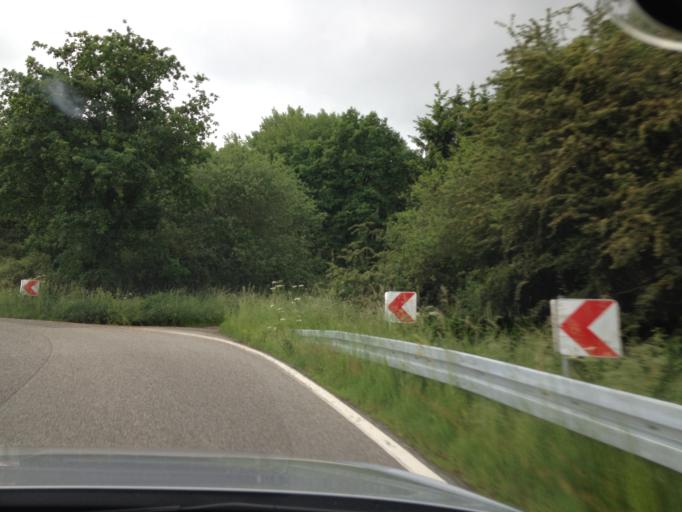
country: DE
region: Saarland
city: Freisen
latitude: 49.5175
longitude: 7.2465
